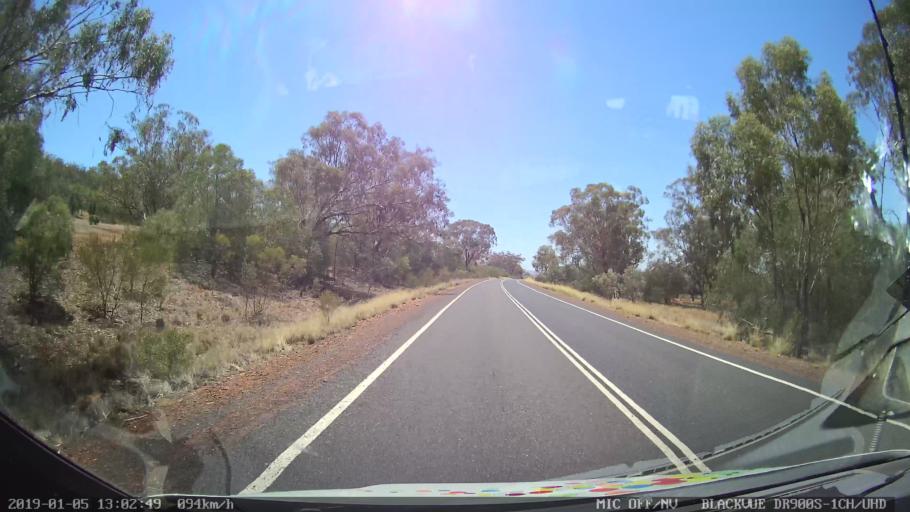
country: AU
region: New South Wales
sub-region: Gunnedah
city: Gunnedah
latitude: -31.1130
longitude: 149.8173
